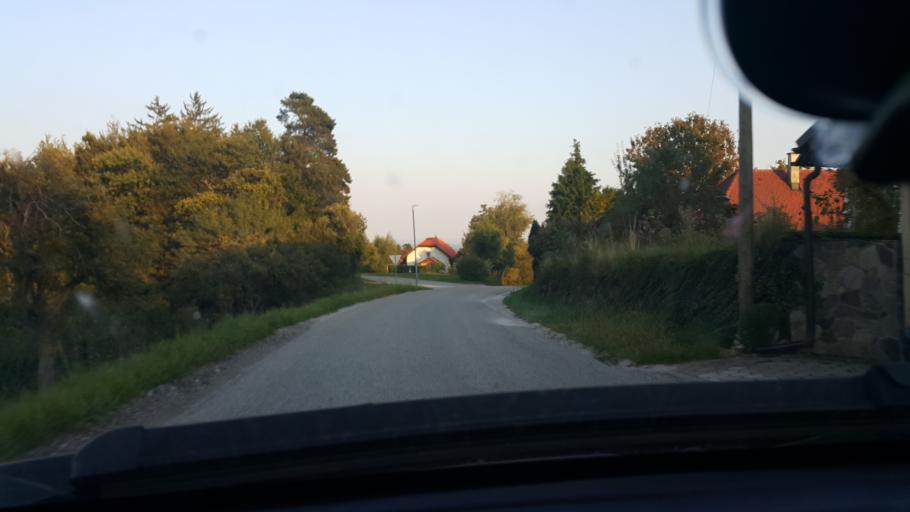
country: SI
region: Race-Fram
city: Fram
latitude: 46.4594
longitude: 15.6187
